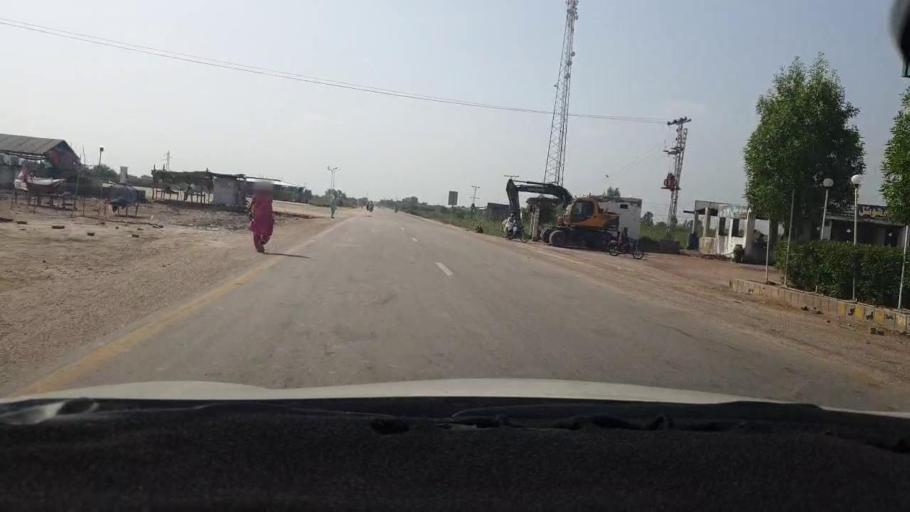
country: PK
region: Sindh
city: Tando Mittha Khan
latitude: 25.8270
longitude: 69.0645
